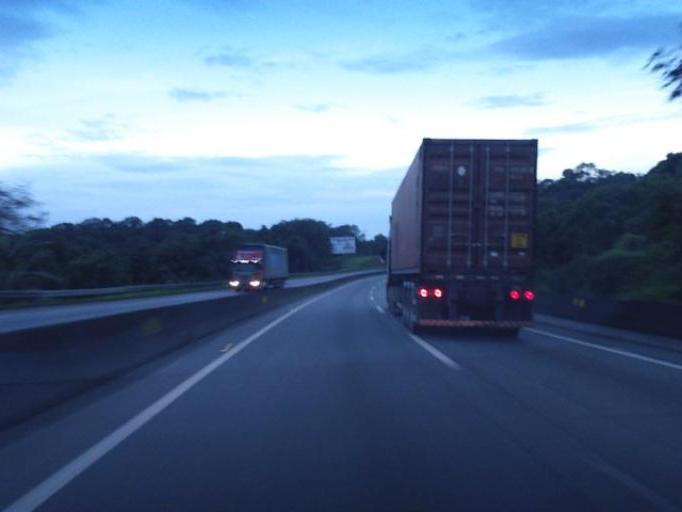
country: BR
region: Santa Catarina
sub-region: Joinville
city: Joinville
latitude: -26.2681
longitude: -48.8961
